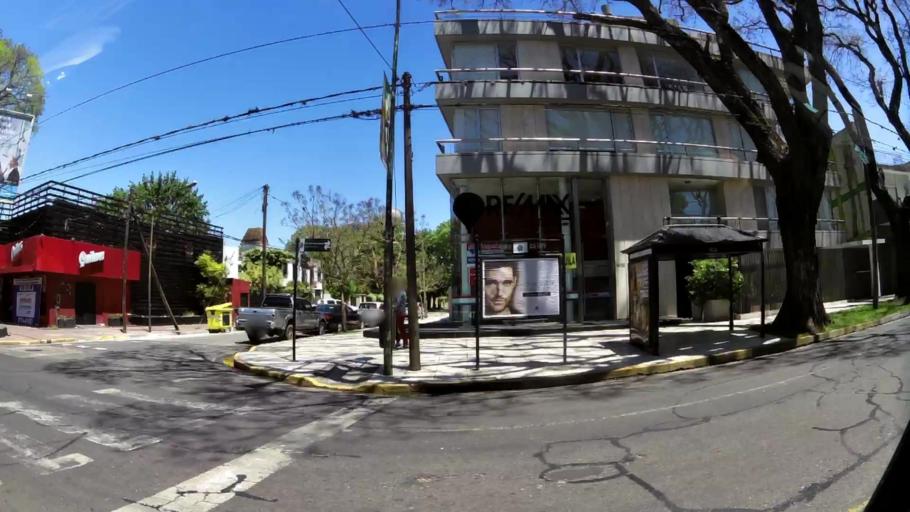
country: AR
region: Buenos Aires
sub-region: Partido de San Isidro
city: San Isidro
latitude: -34.4819
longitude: -58.4912
